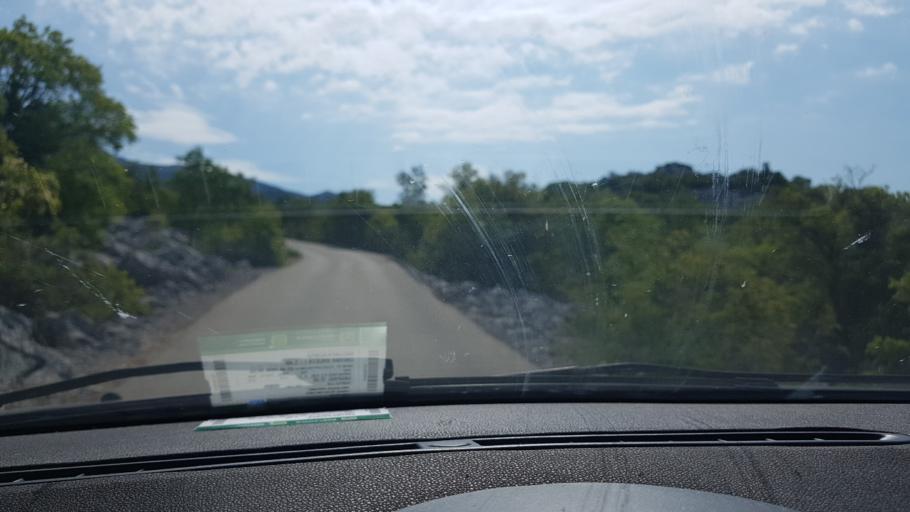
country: HR
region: Licko-Senjska
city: Novalja
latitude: 44.6939
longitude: 14.9167
